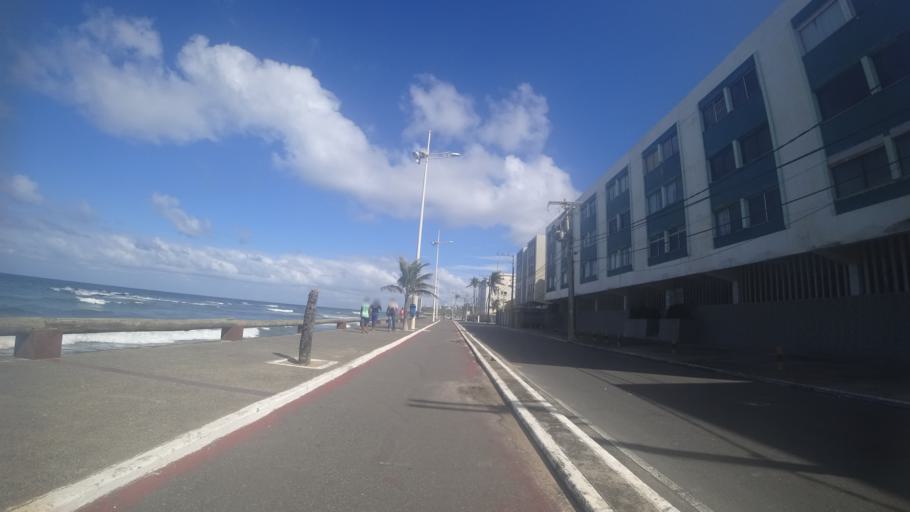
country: BR
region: Bahia
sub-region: Salvador
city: Salvador
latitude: -13.0143
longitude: -38.4696
